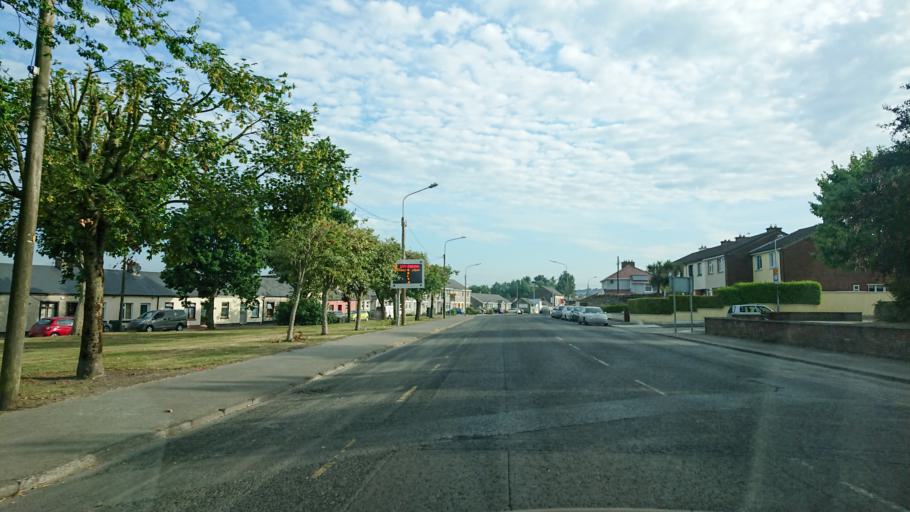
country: IE
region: Munster
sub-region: Waterford
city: Waterford
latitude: 52.2486
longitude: -7.1108
